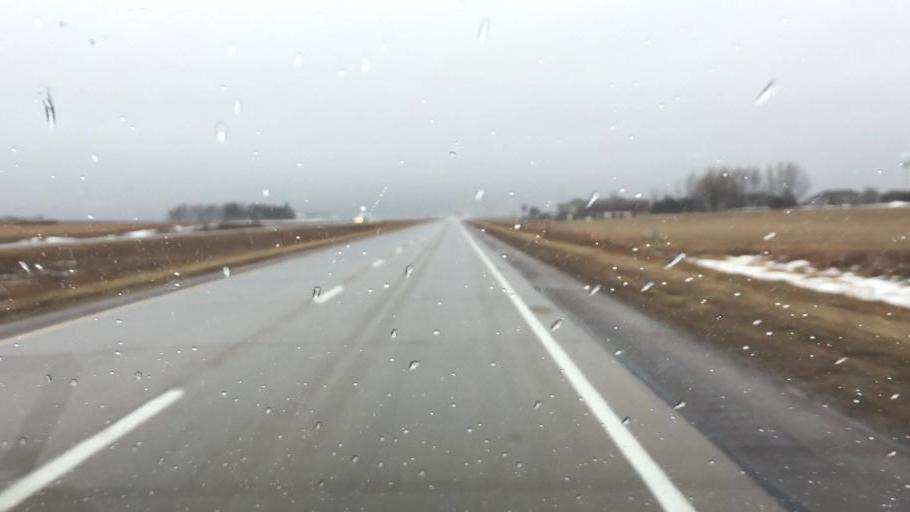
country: US
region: Iowa
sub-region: O'Brien County
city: Sheldon
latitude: 43.0763
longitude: -95.8987
